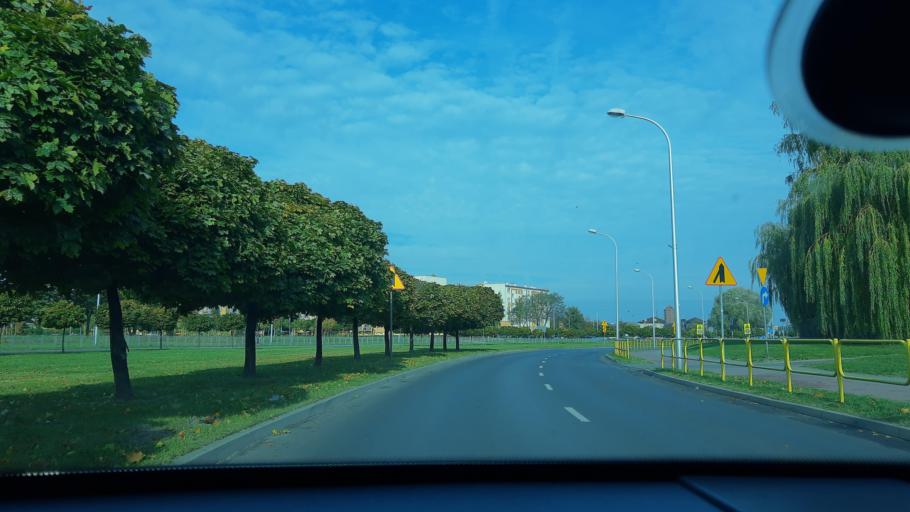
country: PL
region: Lodz Voivodeship
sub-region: Powiat sieradzki
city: Sieradz
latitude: 51.5906
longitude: 18.7156
